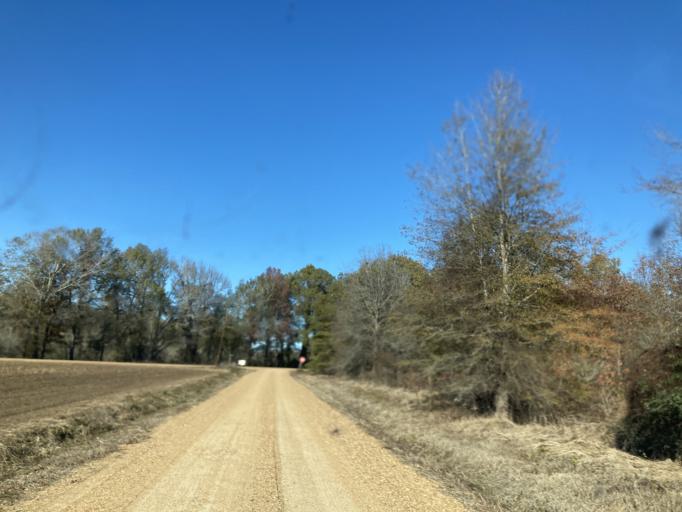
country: US
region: Mississippi
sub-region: Sharkey County
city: Rolling Fork
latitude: 32.7545
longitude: -90.6901
